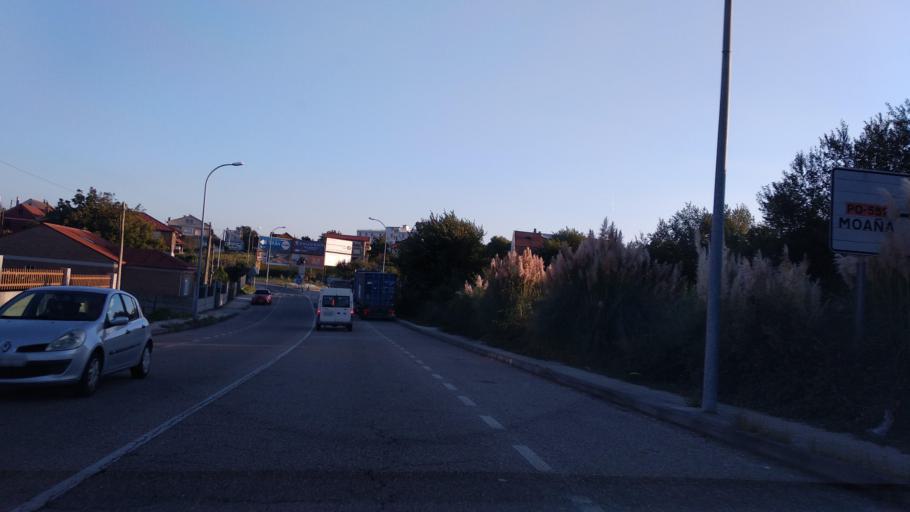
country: ES
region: Galicia
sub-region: Provincia de Pontevedra
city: Cangas
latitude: 42.2640
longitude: -8.7656
